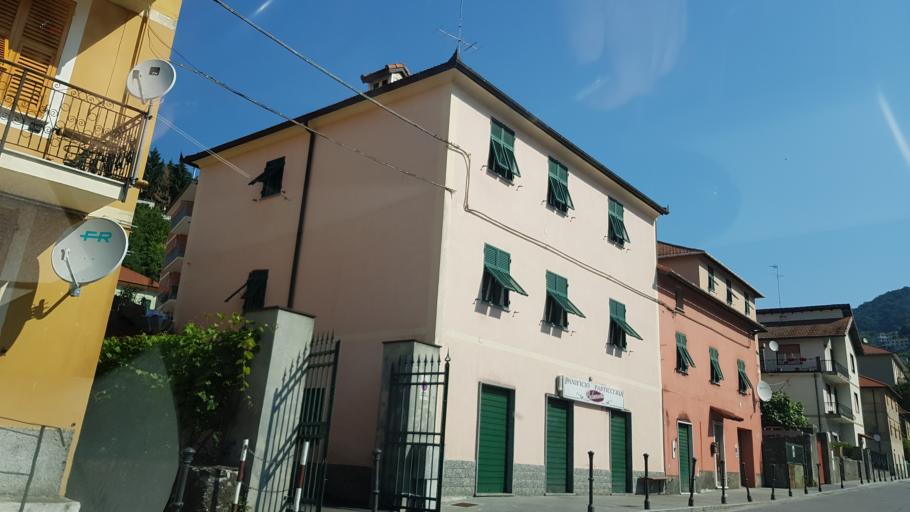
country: IT
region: Liguria
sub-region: Provincia di Genova
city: Serra Ricco
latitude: 44.5103
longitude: 8.9383
